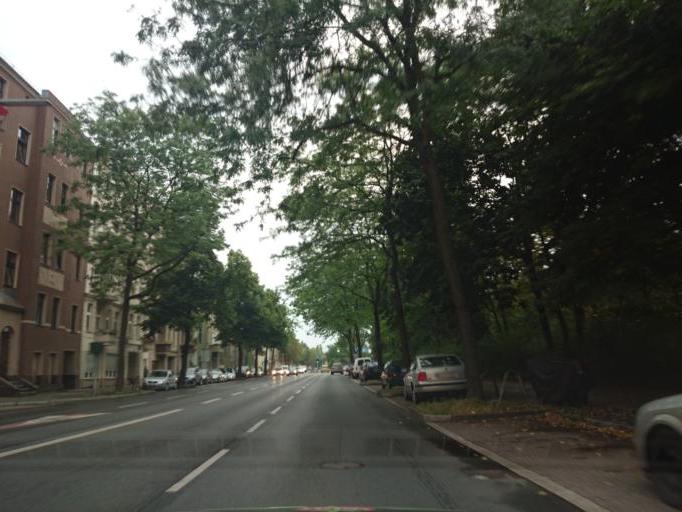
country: DE
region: Berlin
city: Friedenau
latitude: 52.4643
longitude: 13.3162
